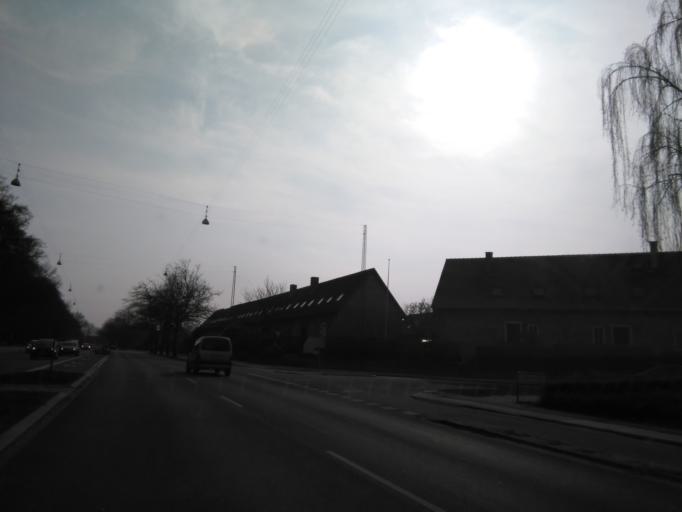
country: DK
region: Central Jutland
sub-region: Arhus Kommune
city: Arhus
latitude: 56.1823
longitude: 10.2179
